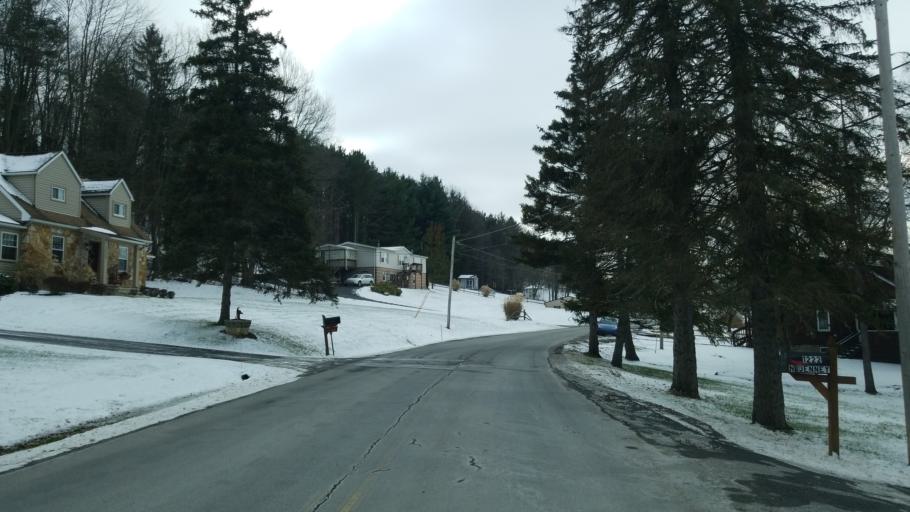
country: US
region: Pennsylvania
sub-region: Clearfield County
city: Sandy
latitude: 41.0847
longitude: -78.7490
